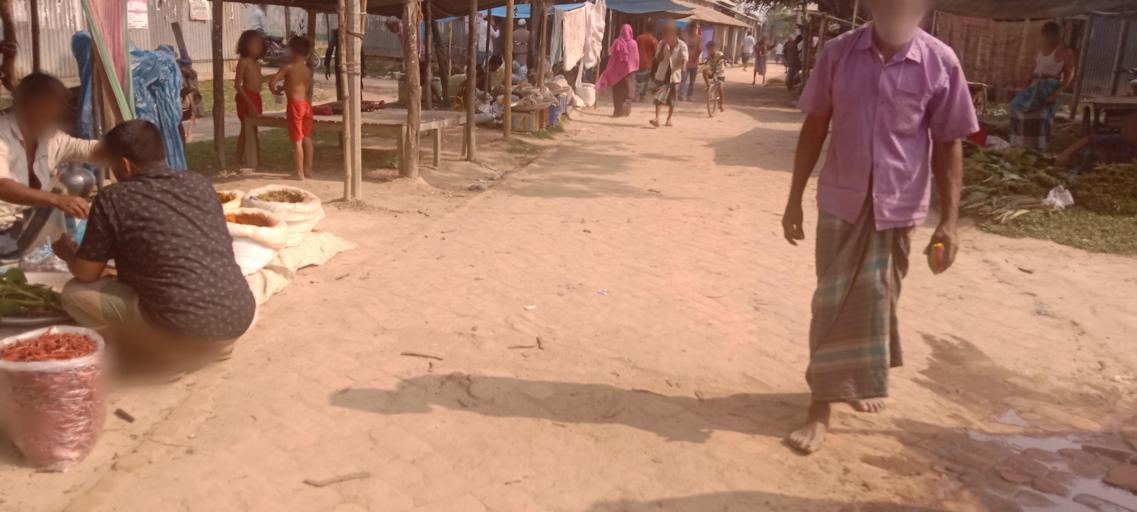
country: BD
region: Dhaka
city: Sakhipur
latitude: 24.3345
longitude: 90.2881
